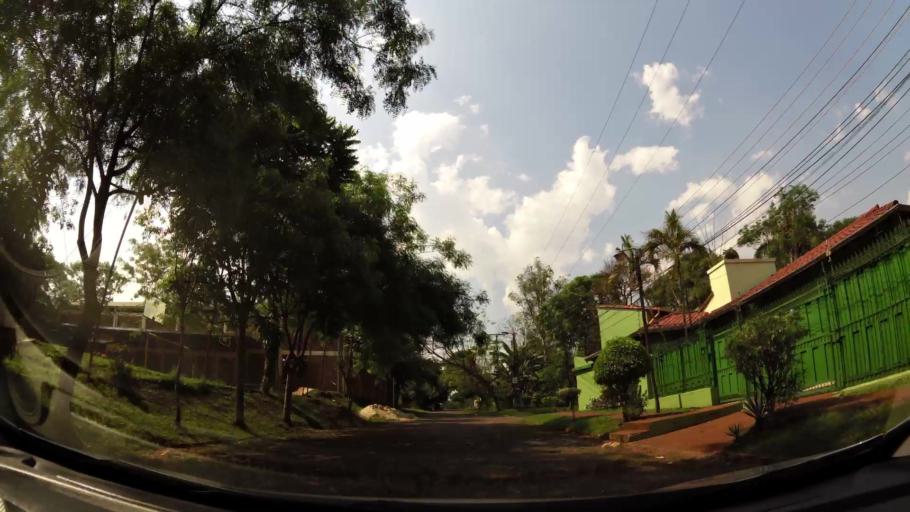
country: PY
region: Alto Parana
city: Ciudad del Este
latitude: -25.5149
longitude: -54.6234
